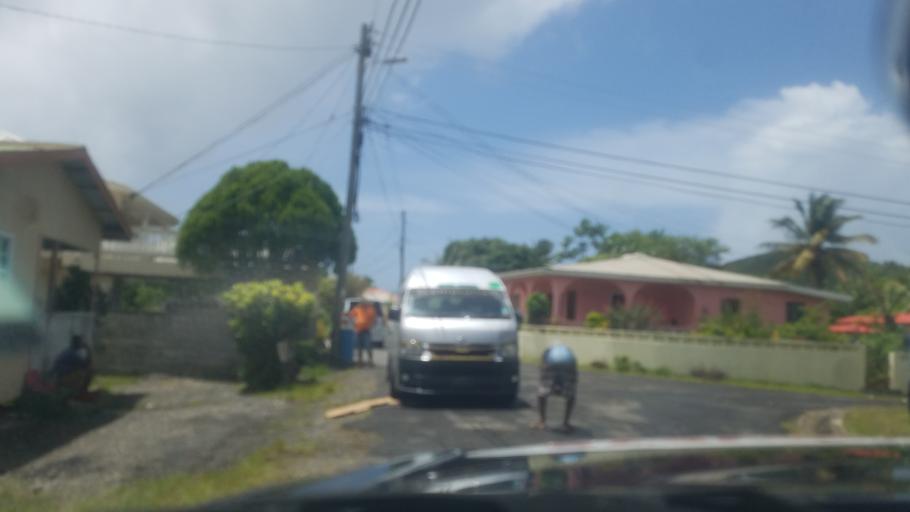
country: LC
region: Laborie Quarter
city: Laborie
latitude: 13.7518
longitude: -60.9666
